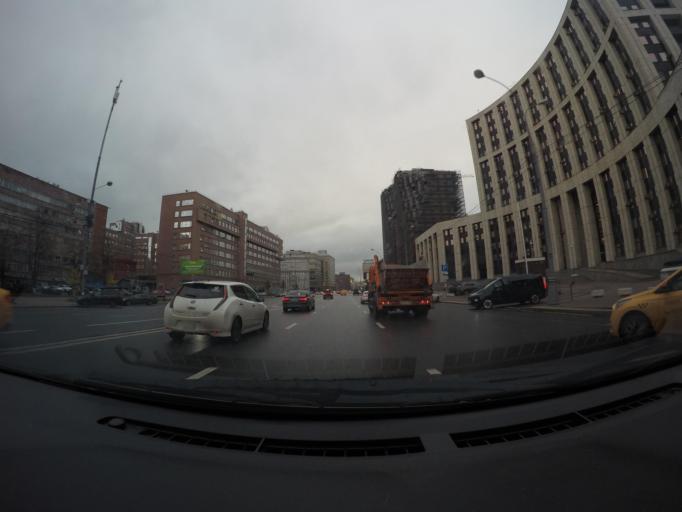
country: RU
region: Moscow
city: Moscow
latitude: 55.7722
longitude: 37.6461
